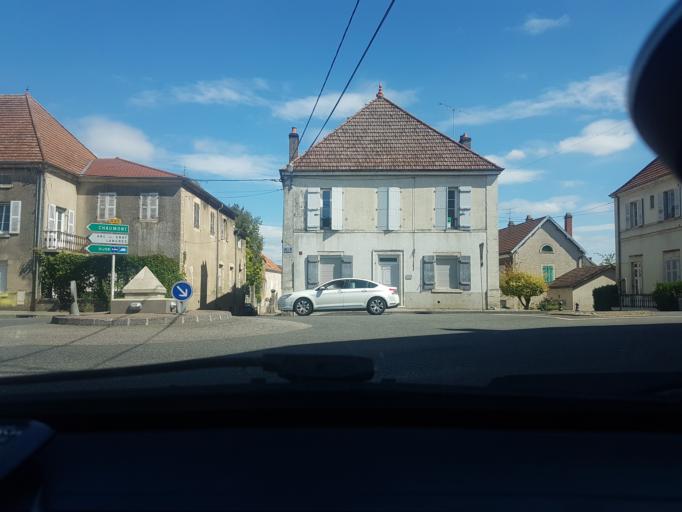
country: FR
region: Franche-Comte
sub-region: Departement de la Haute-Saone
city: Gray
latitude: 47.4507
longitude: 5.5905
